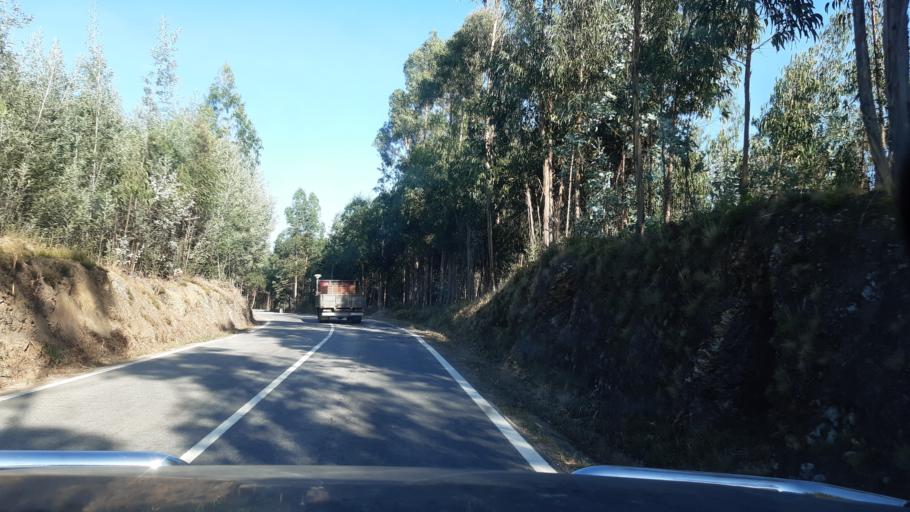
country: PT
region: Aveiro
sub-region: Agueda
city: Aguada de Cima
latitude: 40.5645
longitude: -8.3835
